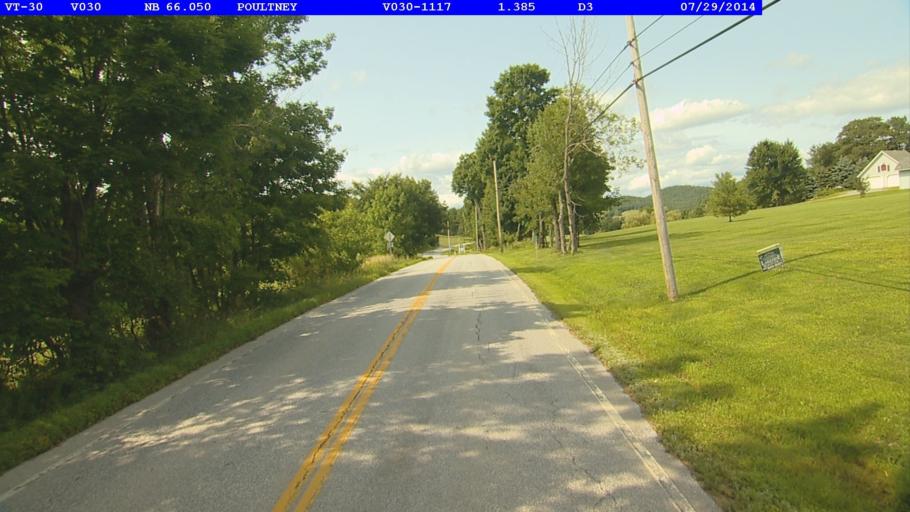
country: US
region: Vermont
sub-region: Rutland County
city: Poultney
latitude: 43.4833
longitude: -73.2027
